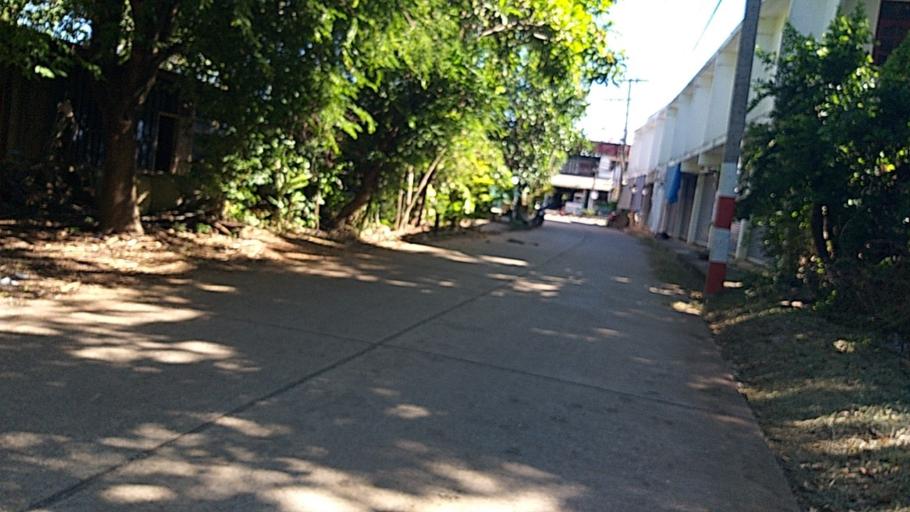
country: TH
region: Chaiyaphum
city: Ban Thaen
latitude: 16.4077
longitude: 102.3502
